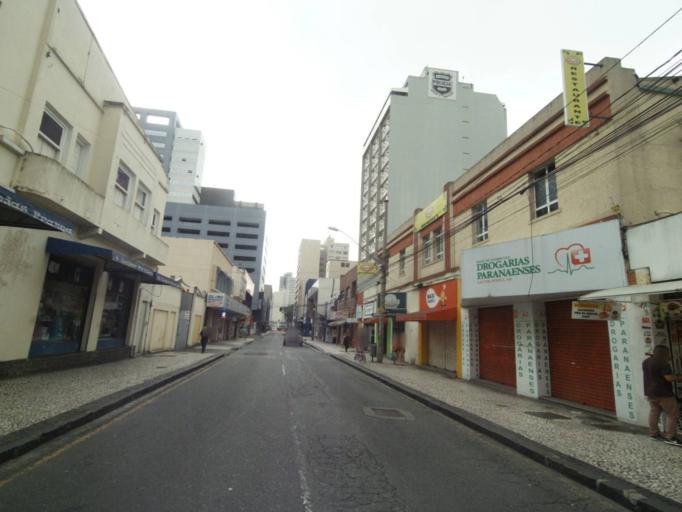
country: BR
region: Parana
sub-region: Curitiba
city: Curitiba
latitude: -25.4320
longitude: -49.2680
